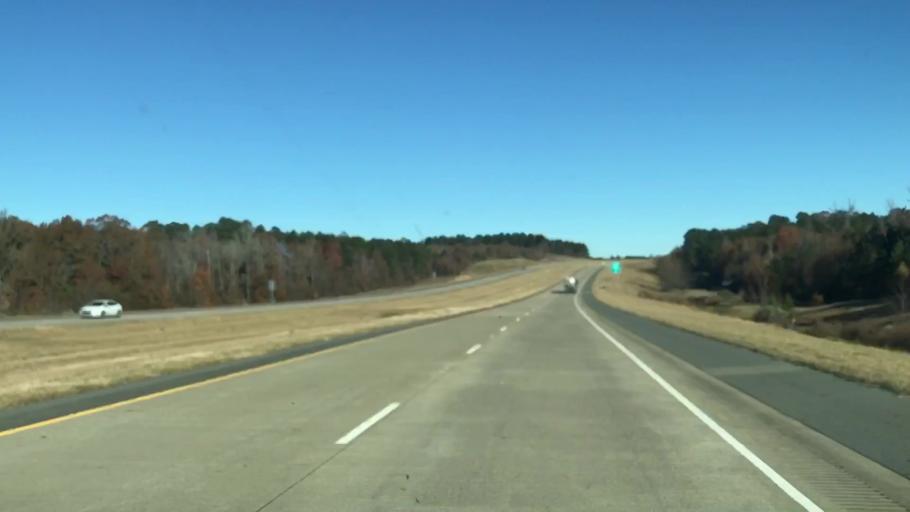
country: US
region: Louisiana
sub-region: Caddo Parish
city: Vivian
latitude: 32.9826
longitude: -93.9103
